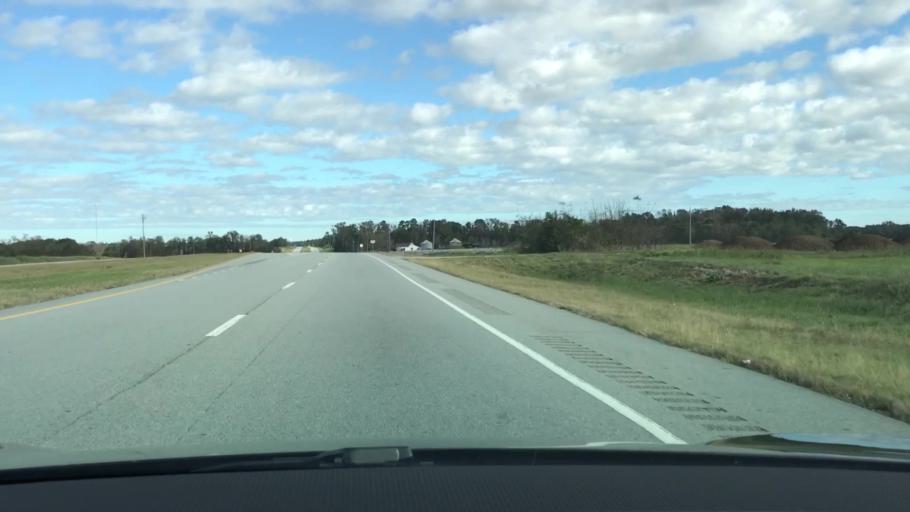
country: US
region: Georgia
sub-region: Jefferson County
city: Wadley
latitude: 32.8283
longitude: -82.4023
